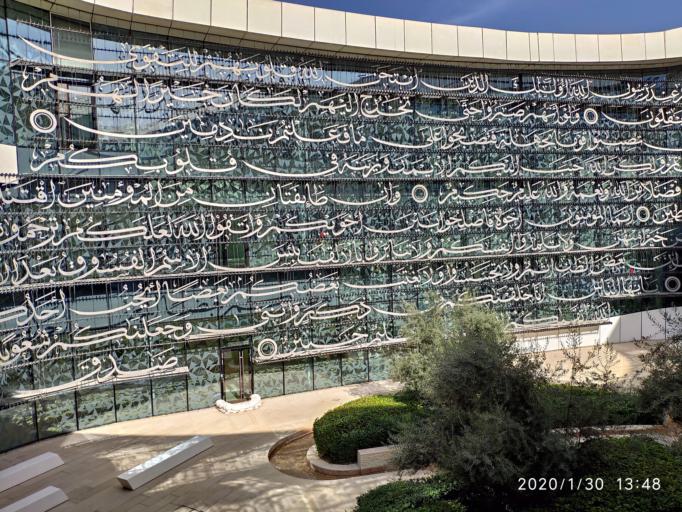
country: QA
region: Baladiyat ar Rayyan
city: Ar Rayyan
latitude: 25.3171
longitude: 51.4474
